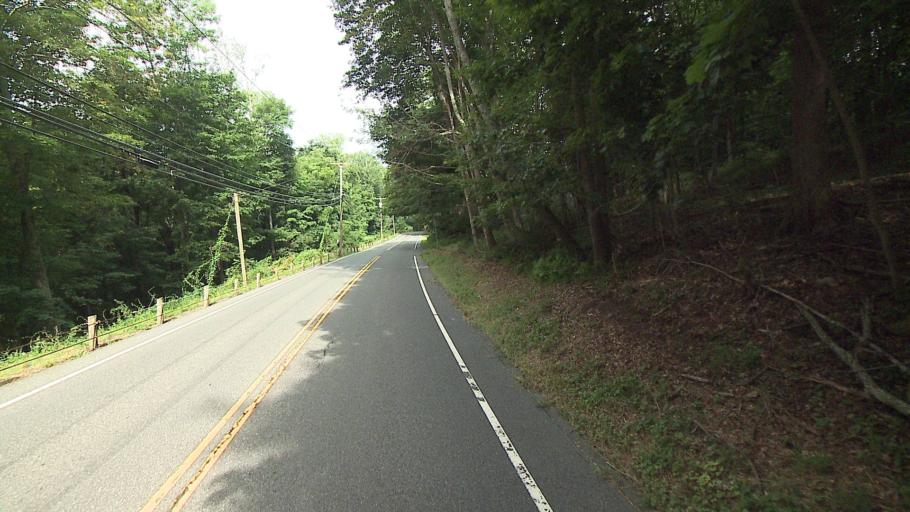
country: US
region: Connecticut
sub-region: Litchfield County
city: New Preston
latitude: 41.6246
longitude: -73.3052
